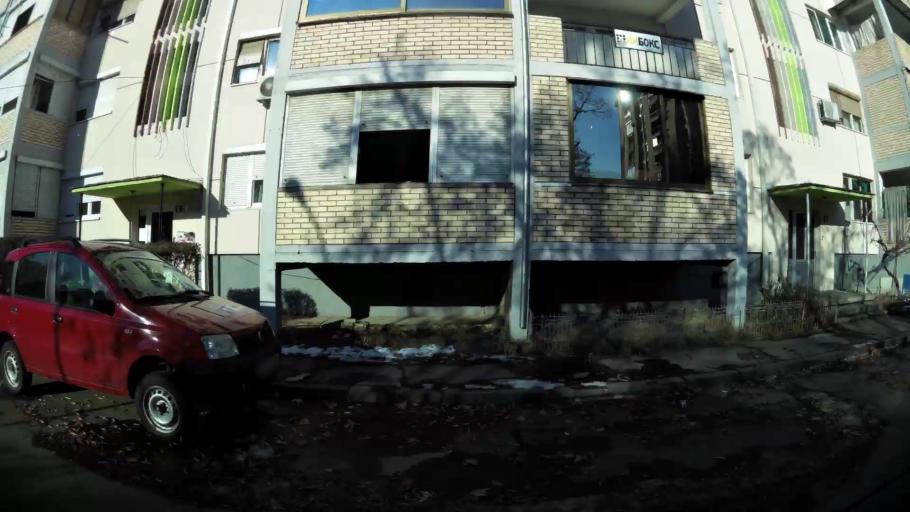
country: MK
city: Krushopek
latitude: 42.0057
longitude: 21.3863
